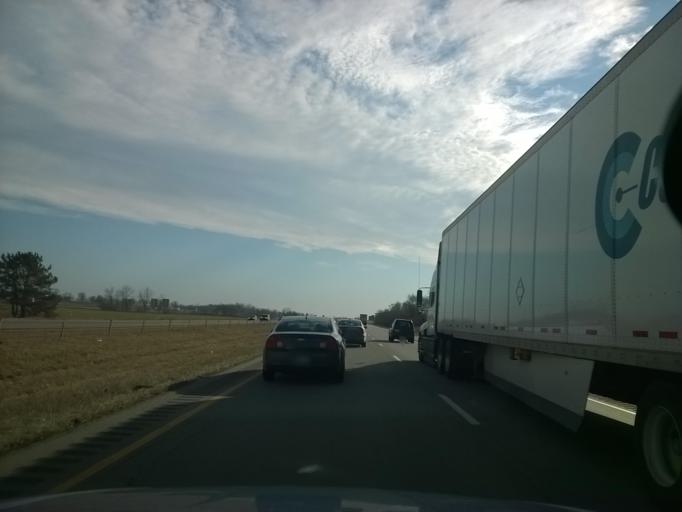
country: US
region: Indiana
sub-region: Johnson County
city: Edinburgh
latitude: 39.3737
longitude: -85.9428
